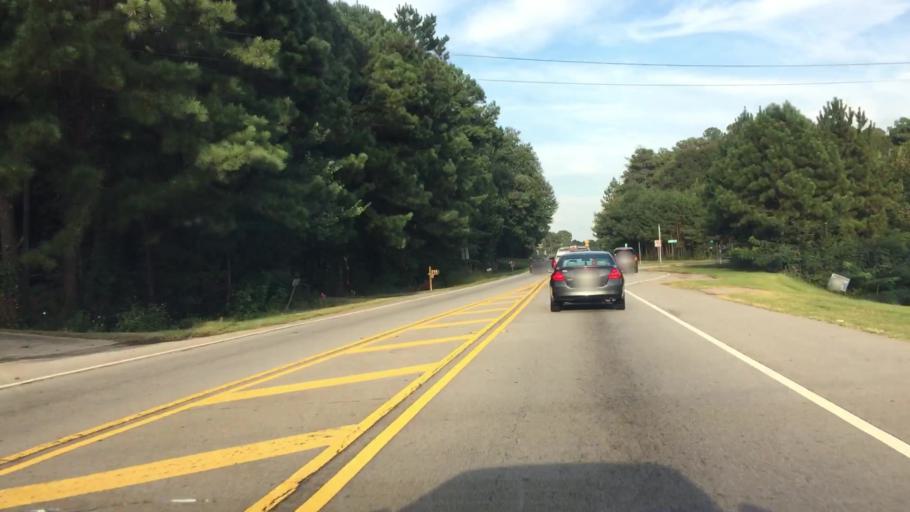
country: US
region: Georgia
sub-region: Henry County
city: Stockbridge
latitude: 33.5402
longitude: -84.2000
